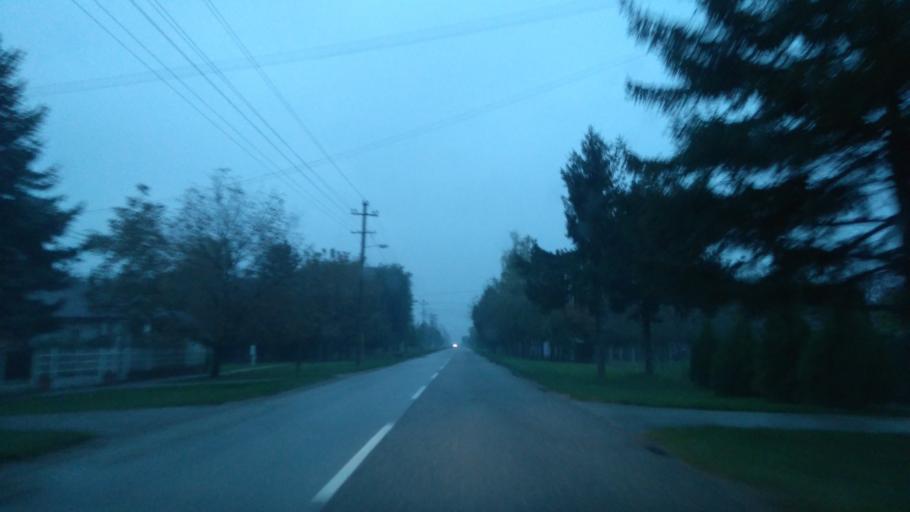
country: RS
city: Backo Petrovo Selo
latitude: 45.7161
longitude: 20.0912
